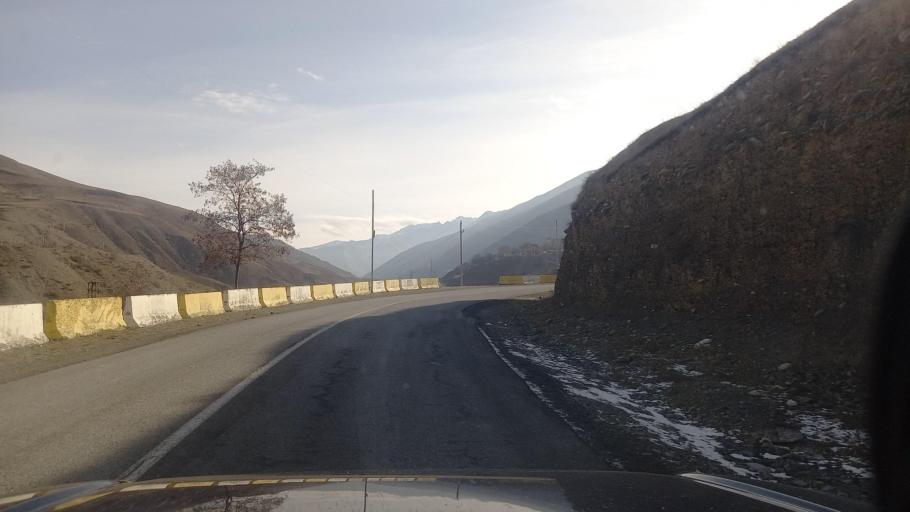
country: RU
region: Ingushetiya
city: Dzhayrakh
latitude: 42.8299
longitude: 44.6683
